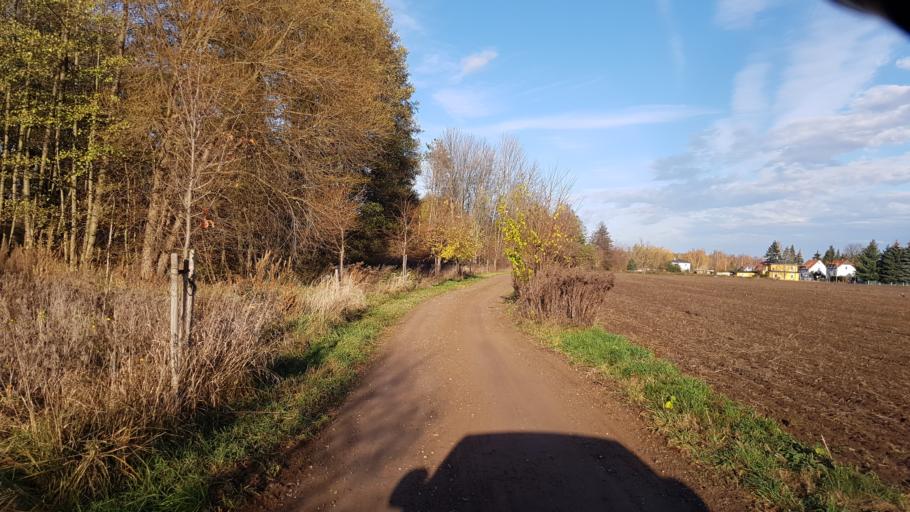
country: DE
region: Brandenburg
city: Ortrand
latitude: 51.3698
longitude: 13.7656
